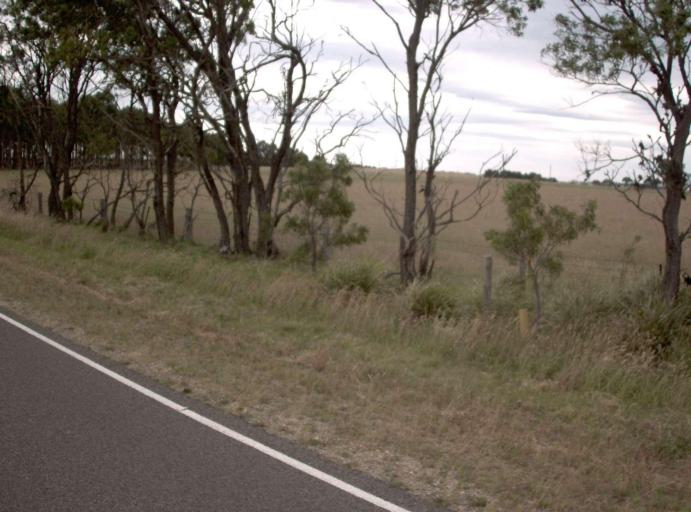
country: AU
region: Victoria
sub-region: East Gippsland
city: Bairnsdale
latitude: -37.9664
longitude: 147.4831
